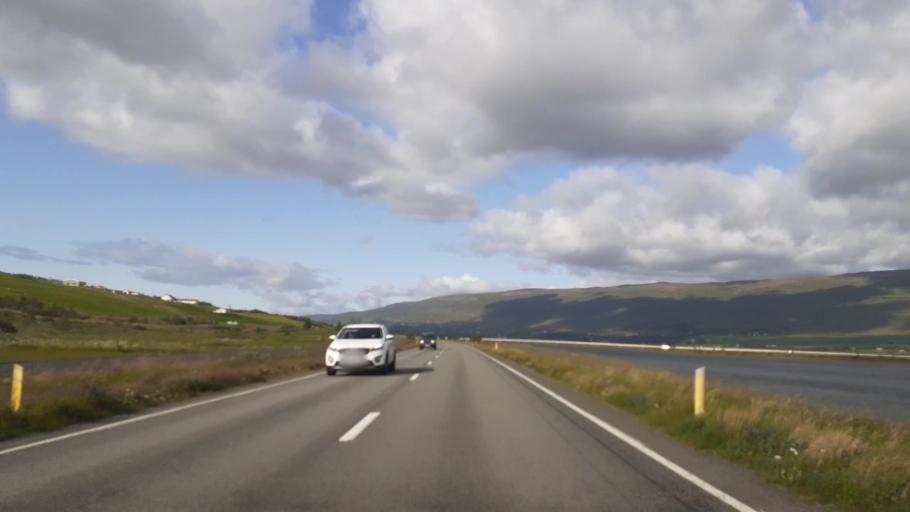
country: IS
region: Northeast
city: Akureyri
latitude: 65.6166
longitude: -18.0772
